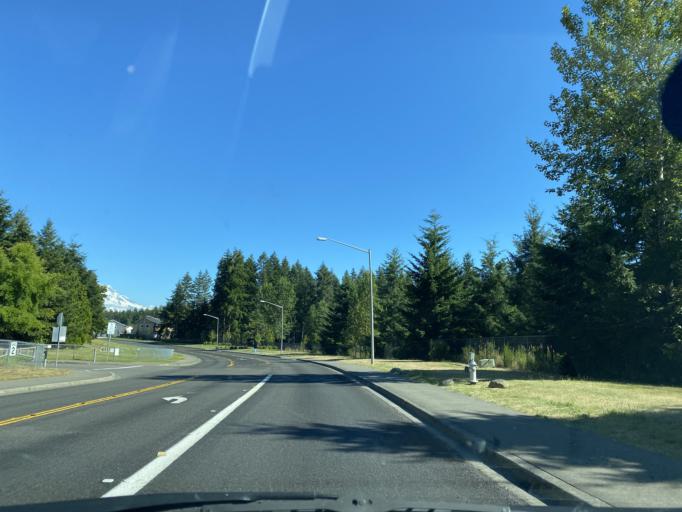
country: US
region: Washington
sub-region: Pierce County
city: Graham
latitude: 47.0892
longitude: -122.2657
